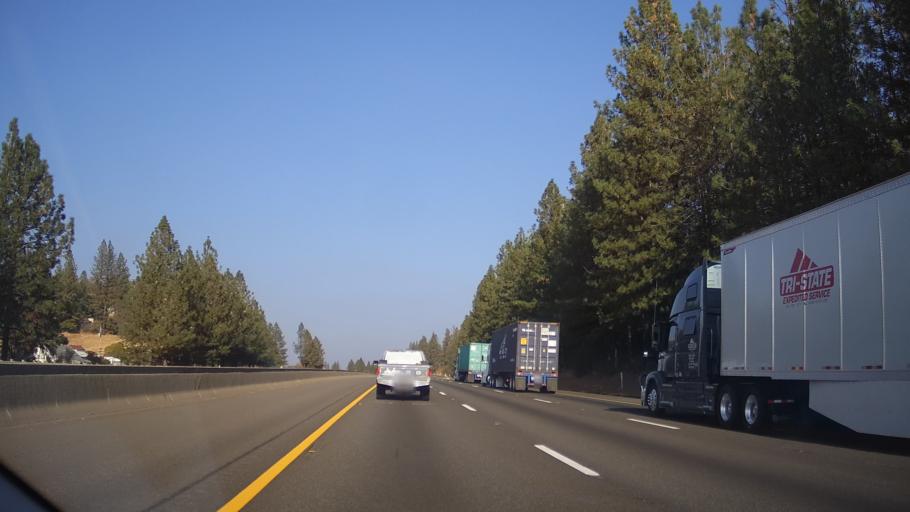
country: US
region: California
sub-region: Placer County
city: Meadow Vista
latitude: 38.9877
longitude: -121.0032
